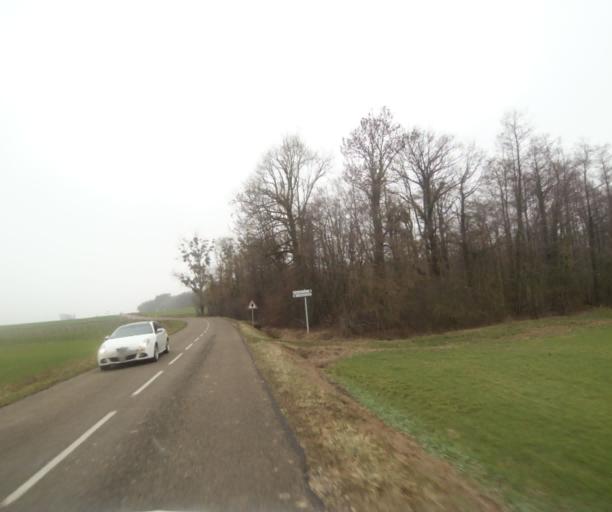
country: FR
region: Champagne-Ardenne
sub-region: Departement de la Haute-Marne
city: Bienville
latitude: 48.5224
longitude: 5.0429
